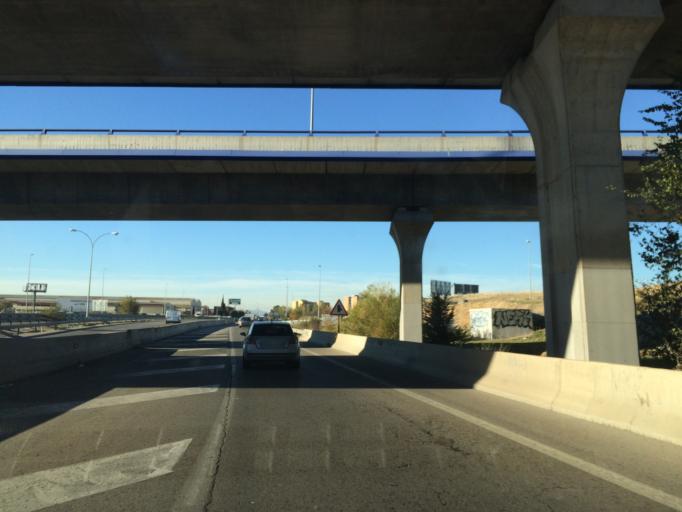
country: ES
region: Madrid
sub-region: Provincia de Madrid
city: Mostoles
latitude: 40.3078
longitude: -3.8332
